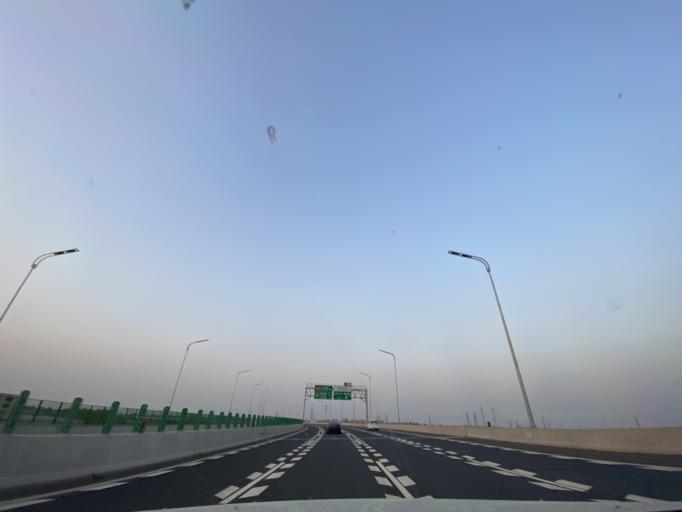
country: CN
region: Beijing
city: Xingfeng
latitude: 39.6949
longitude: 116.3755
